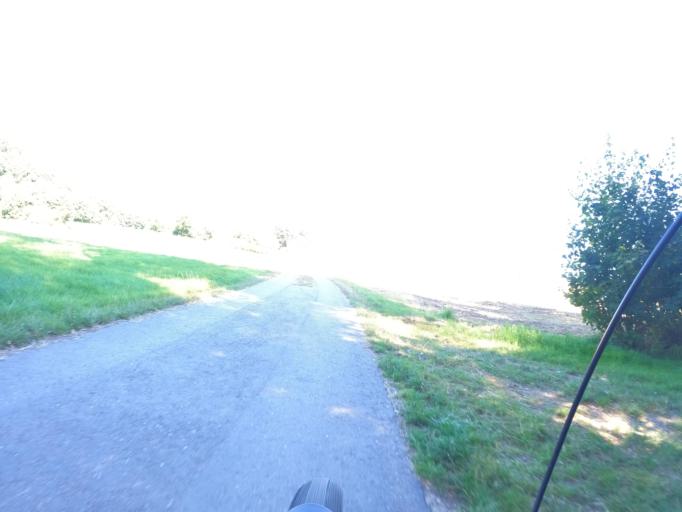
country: DE
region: Schleswig-Holstein
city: Steinberg
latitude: 54.7884
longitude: 9.7879
